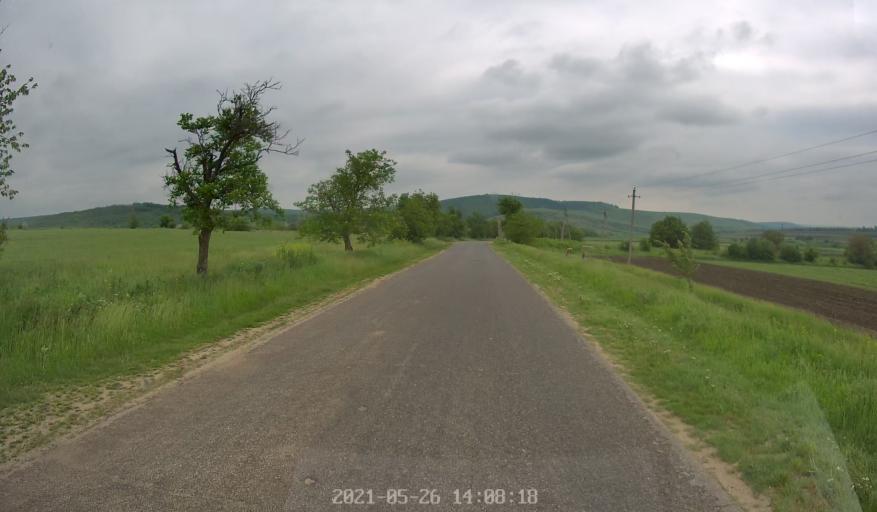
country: MD
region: Hincesti
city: Dancu
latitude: 46.7388
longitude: 28.3593
